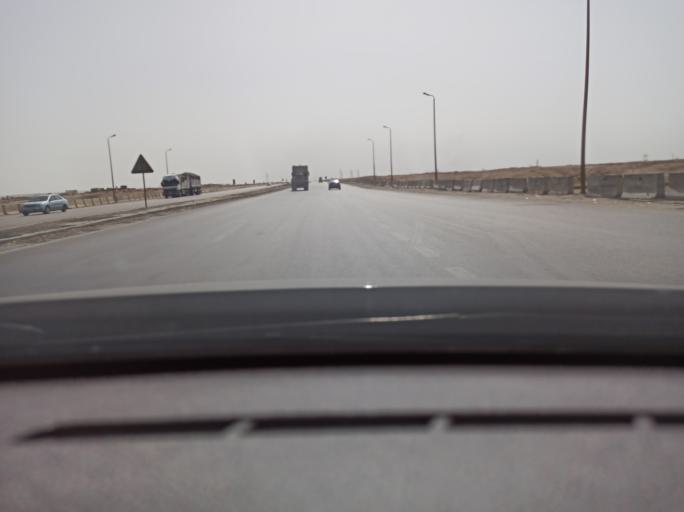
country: EG
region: Muhafazat al Qahirah
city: Halwan
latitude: 29.7884
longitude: 31.3490
